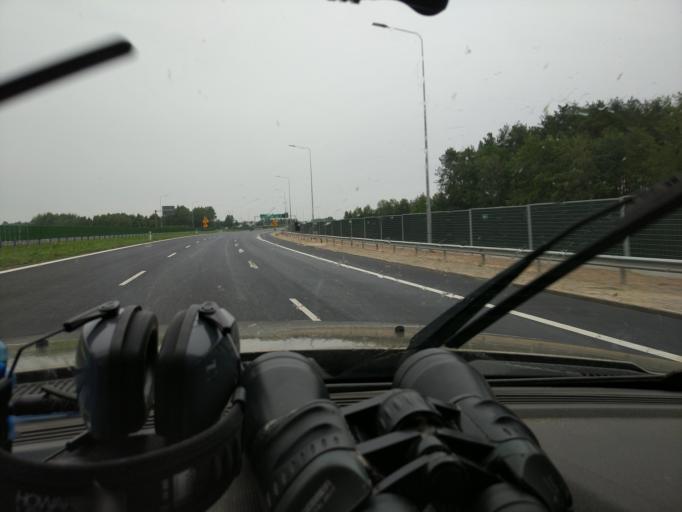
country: PL
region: Masovian Voivodeship
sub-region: Powiat wolominski
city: Slupno
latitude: 52.3486
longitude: 21.1583
